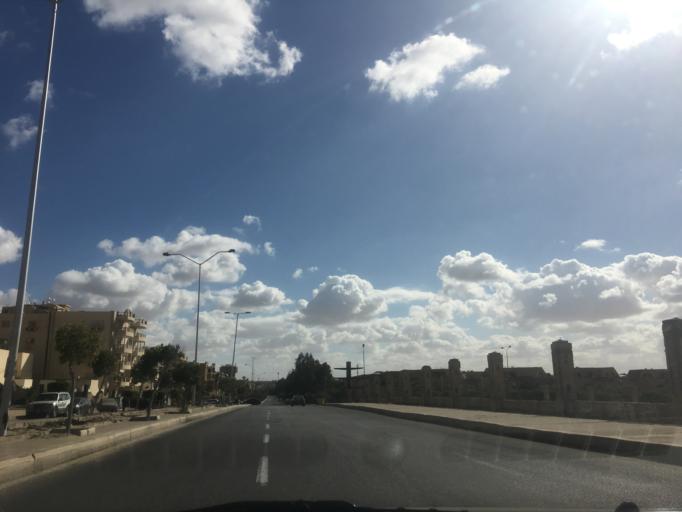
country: EG
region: Al Jizah
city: Madinat Sittah Uktubar
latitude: 30.0001
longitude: 30.9743
